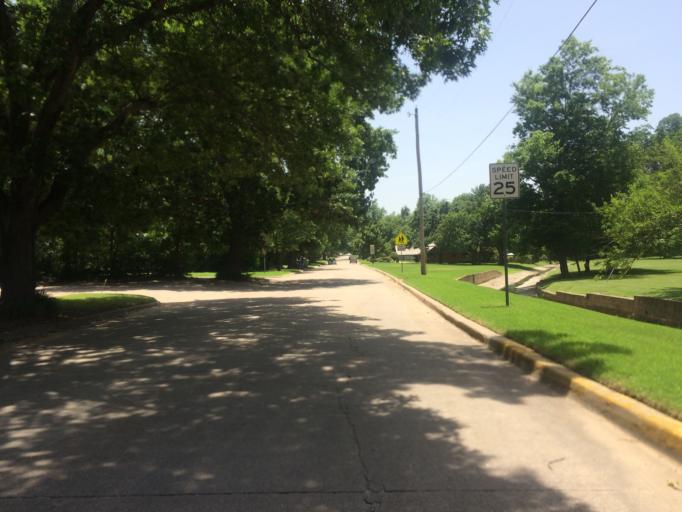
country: US
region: Oklahoma
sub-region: Cleveland County
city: Norman
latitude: 35.2111
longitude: -97.4545
